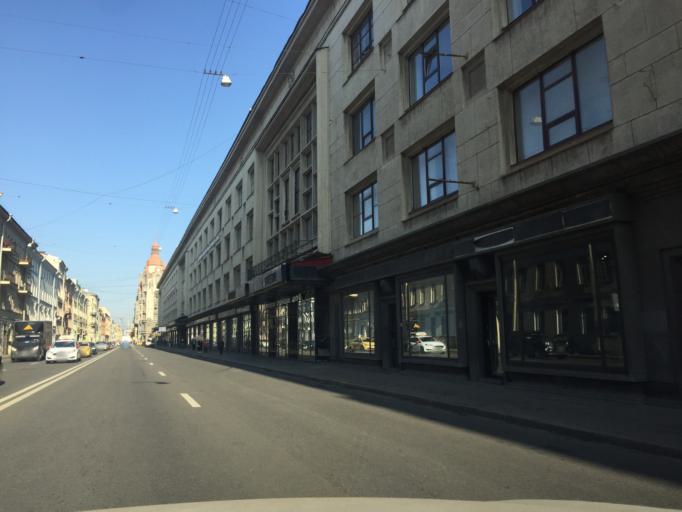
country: RU
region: St.-Petersburg
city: Saint Petersburg
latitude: 59.9204
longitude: 30.3080
